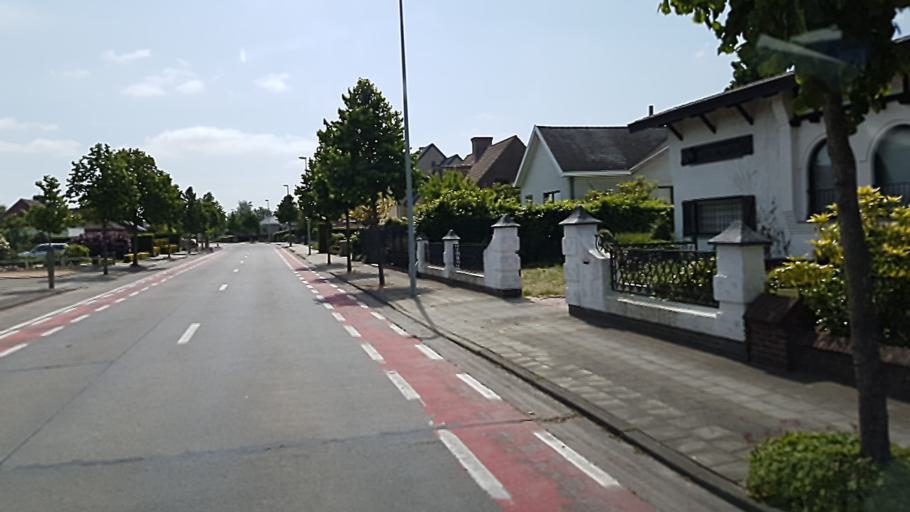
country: BE
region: Flanders
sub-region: Provincie West-Vlaanderen
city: Wevelgem
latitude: 50.8371
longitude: 3.2050
